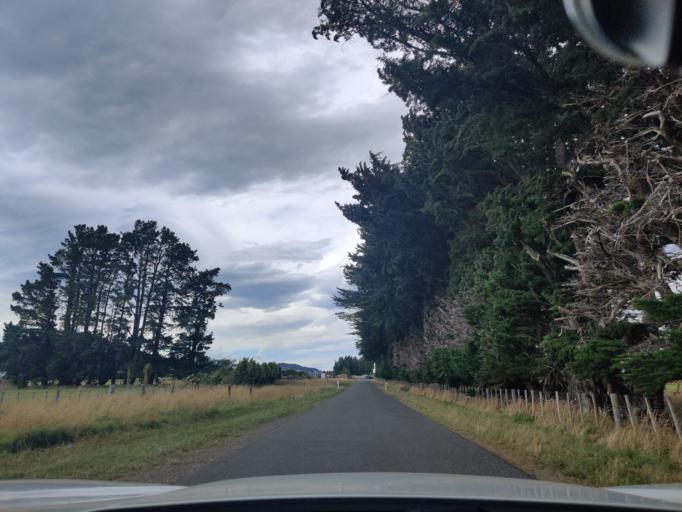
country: NZ
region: Wellington
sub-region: Masterton District
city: Masterton
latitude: -41.0201
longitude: 175.4626
